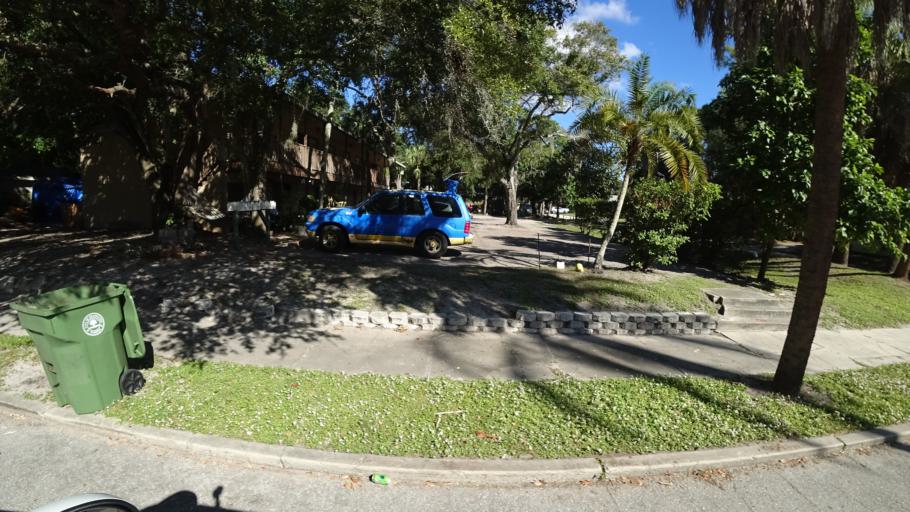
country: US
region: Florida
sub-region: Manatee County
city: Bradenton
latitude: 27.4929
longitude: -82.5862
